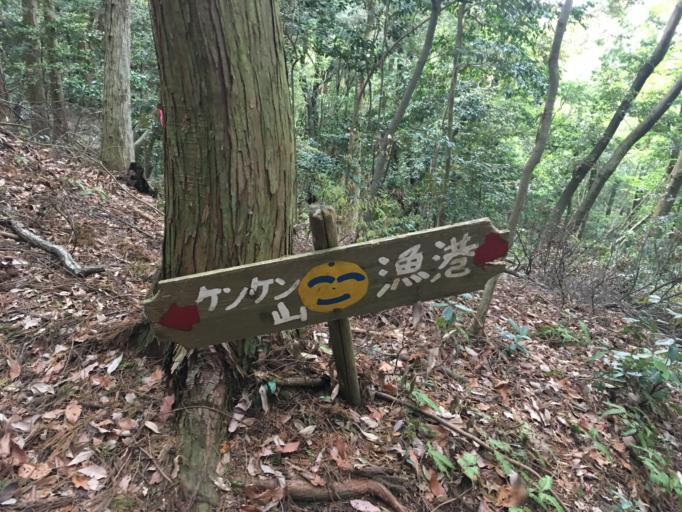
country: JP
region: Shiga Prefecture
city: Omihachiman
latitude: 35.2033
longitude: 136.0574
